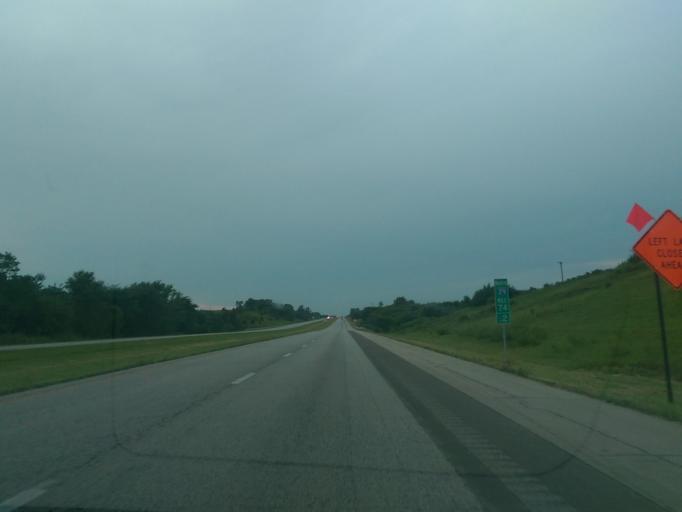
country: US
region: Missouri
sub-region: Holt County
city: Oregon
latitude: 40.0332
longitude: -95.1166
